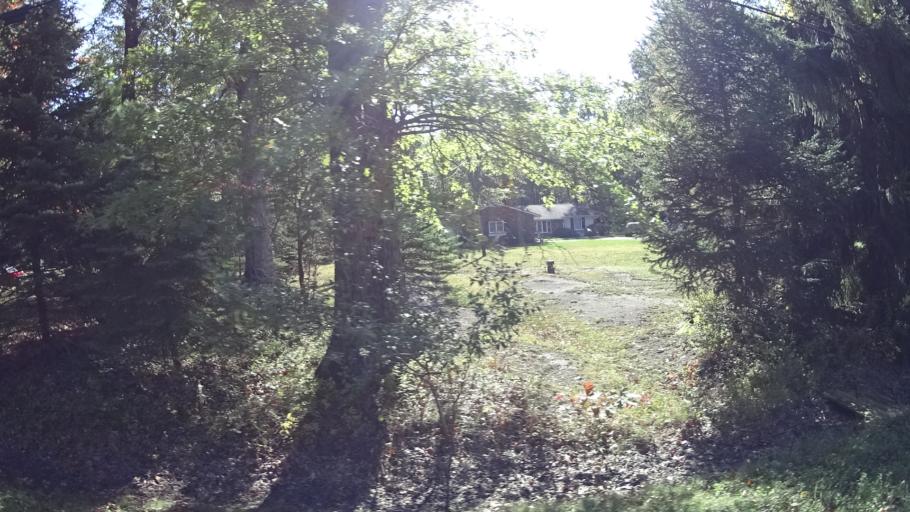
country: US
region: Ohio
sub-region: Lorain County
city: Vermilion-on-the-Lake
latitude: 41.4119
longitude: -82.3219
